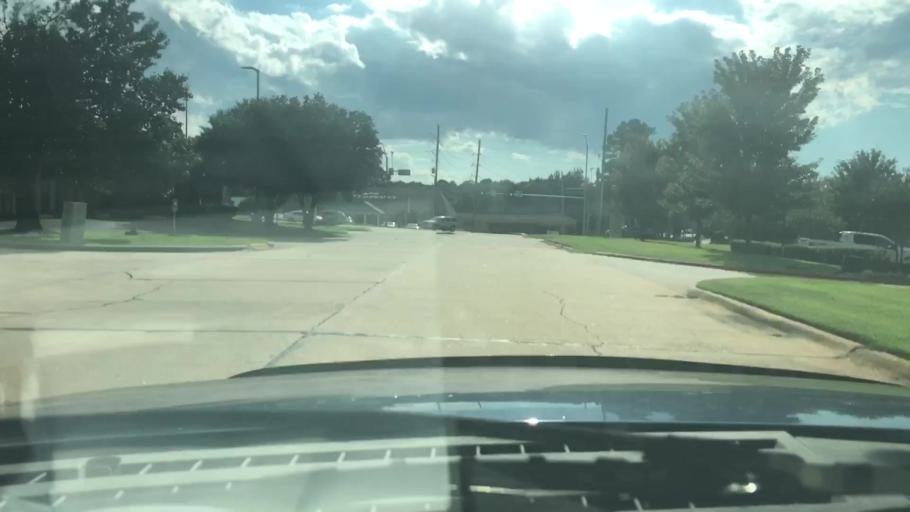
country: US
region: Arkansas
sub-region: Miller County
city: Texarkana
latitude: 33.4692
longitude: -94.0674
